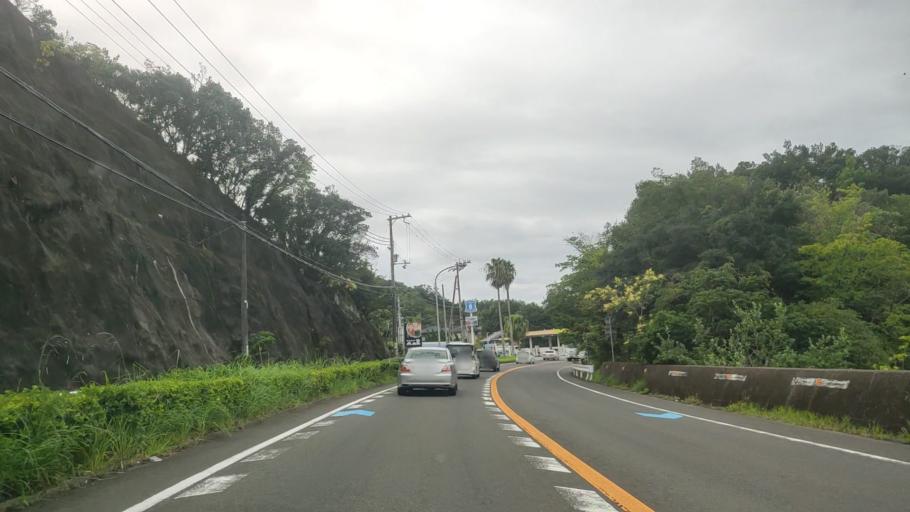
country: JP
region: Wakayama
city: Tanabe
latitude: 33.7029
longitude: 135.3957
